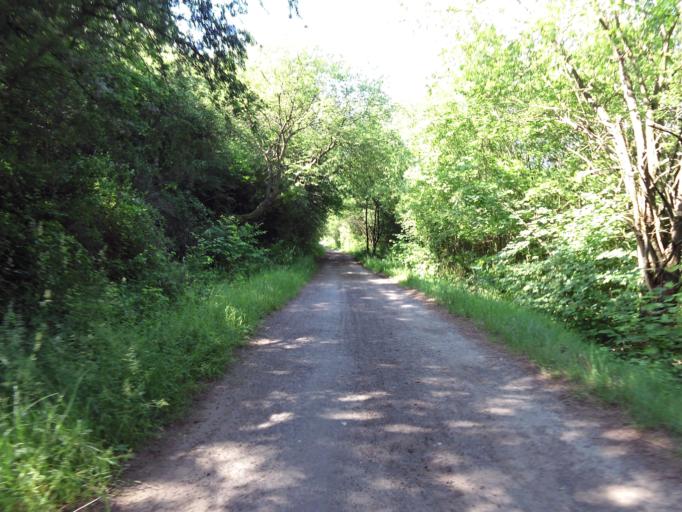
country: DE
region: Rheinland-Pfalz
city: Ebertsheim
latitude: 49.5590
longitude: 8.1091
